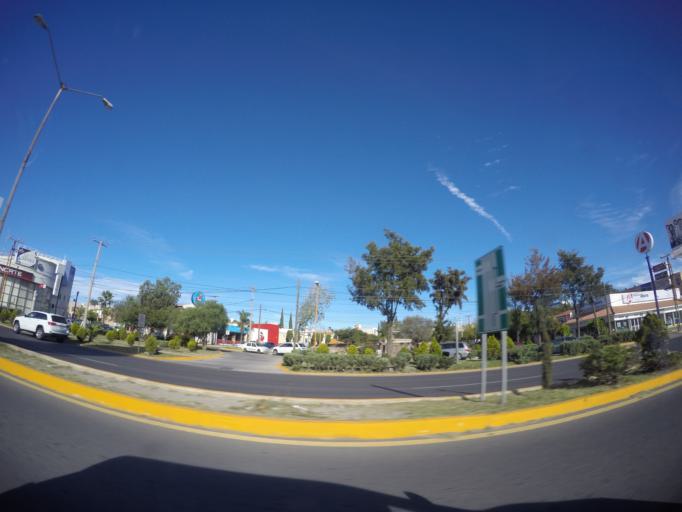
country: MX
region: San Luis Potosi
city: Escalerillas
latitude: 22.1338
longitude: -101.0310
